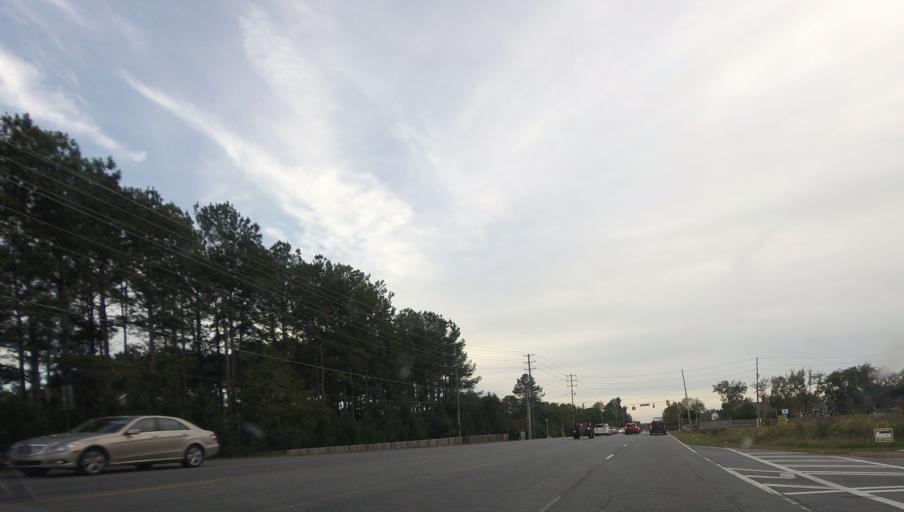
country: US
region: Georgia
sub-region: Houston County
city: Centerville
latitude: 32.5718
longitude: -83.6913
